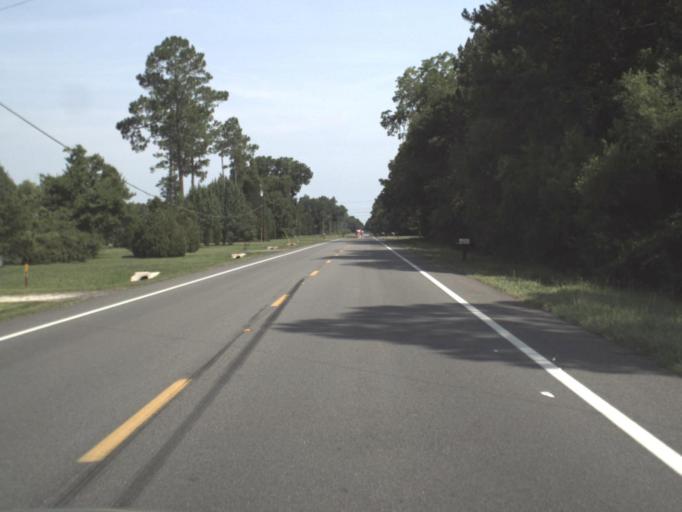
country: US
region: Florida
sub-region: Hamilton County
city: Jasper
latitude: 30.5361
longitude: -82.9720
